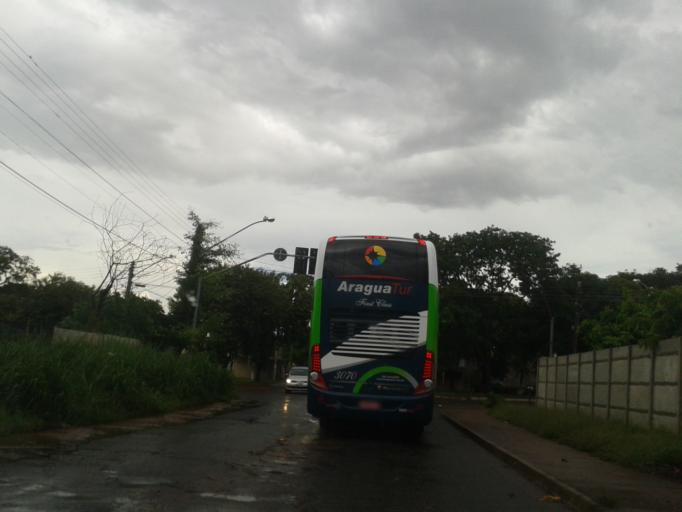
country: BR
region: Goias
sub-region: Goiania
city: Goiania
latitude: -16.6633
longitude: -49.3299
